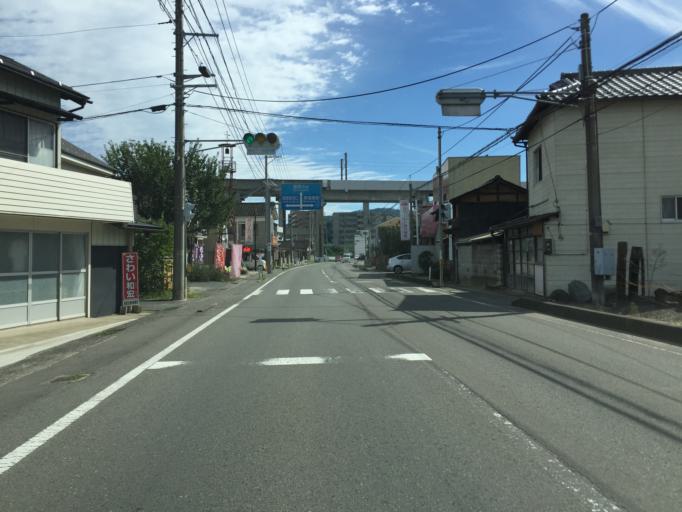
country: JP
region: Fukushima
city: Fukushima-shi
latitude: 37.7439
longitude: 140.4567
